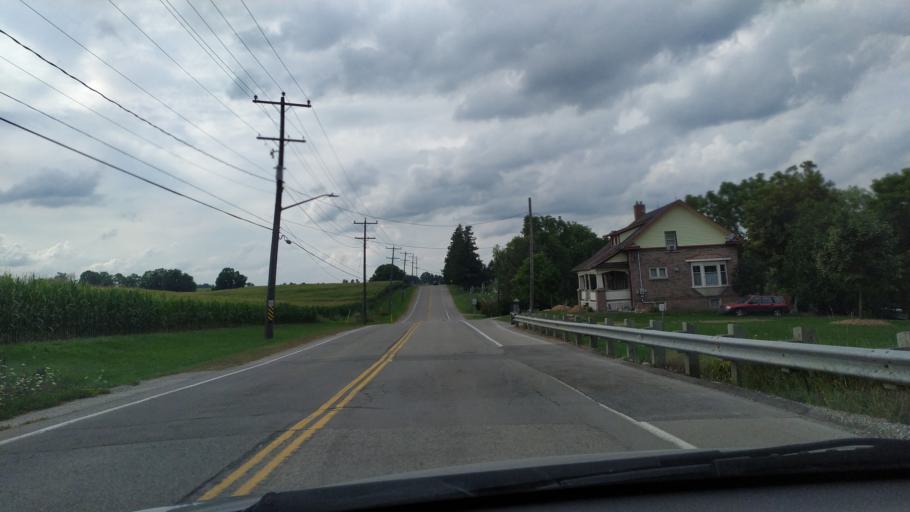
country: CA
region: Ontario
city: Kitchener
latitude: 43.3519
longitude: -80.5396
